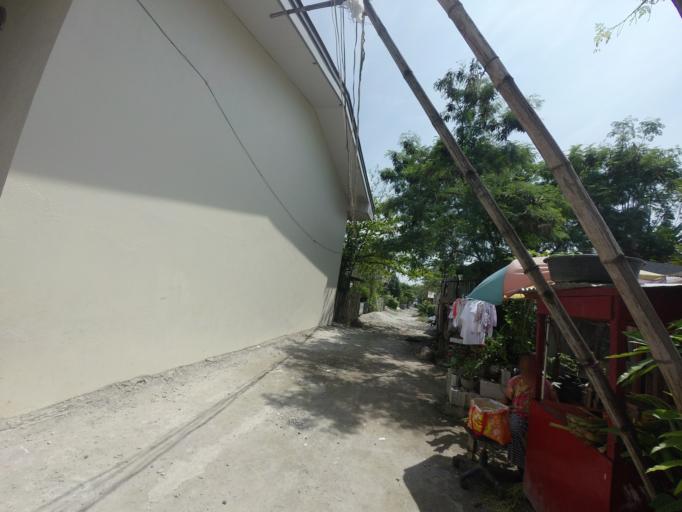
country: PH
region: Calabarzon
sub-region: Province of Rizal
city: Taguig
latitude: 14.5327
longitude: 121.1093
